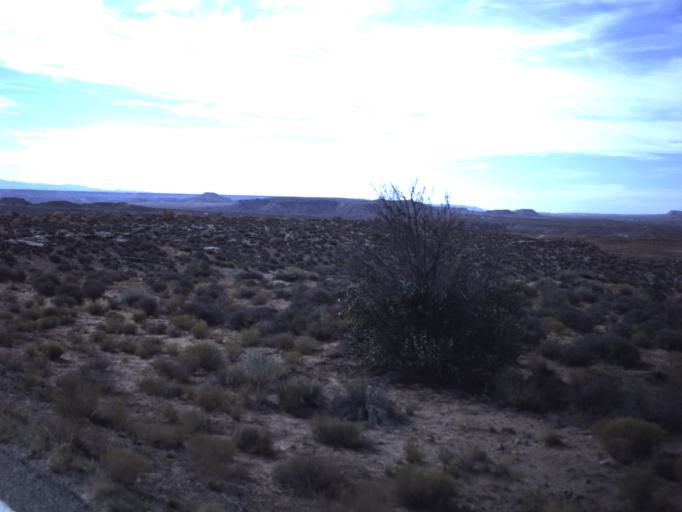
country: US
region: Utah
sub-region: San Juan County
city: Blanding
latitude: 37.3150
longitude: -109.3058
